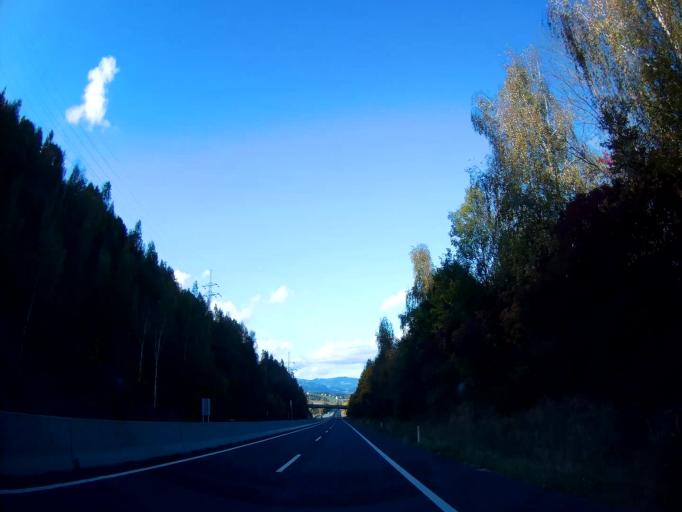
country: AT
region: Carinthia
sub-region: Politischer Bezirk Wolfsberg
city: Sankt Andrae
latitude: 46.7616
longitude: 14.8148
